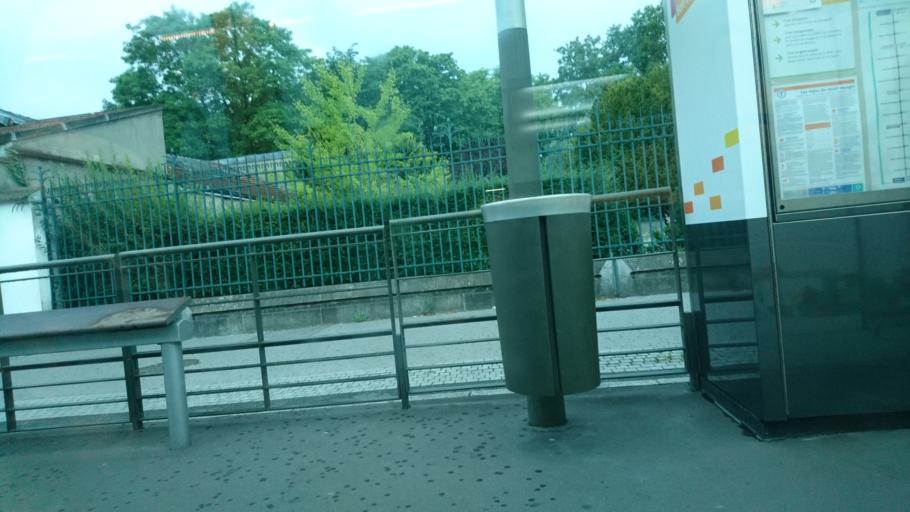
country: FR
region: Ile-de-France
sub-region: Departement de Seine-Saint-Denis
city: Saint-Denis
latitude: 48.9448
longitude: 2.3570
